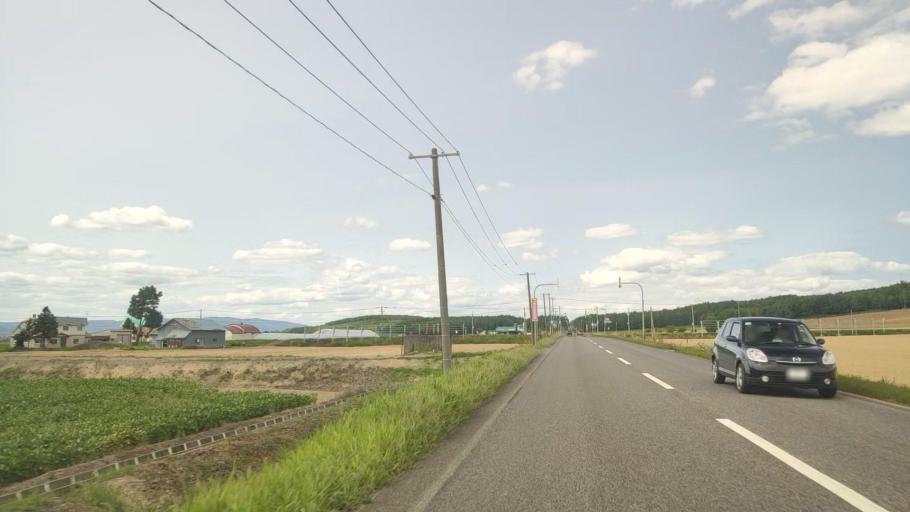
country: JP
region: Hokkaido
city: Nayoro
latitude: 44.2343
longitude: 142.4157
